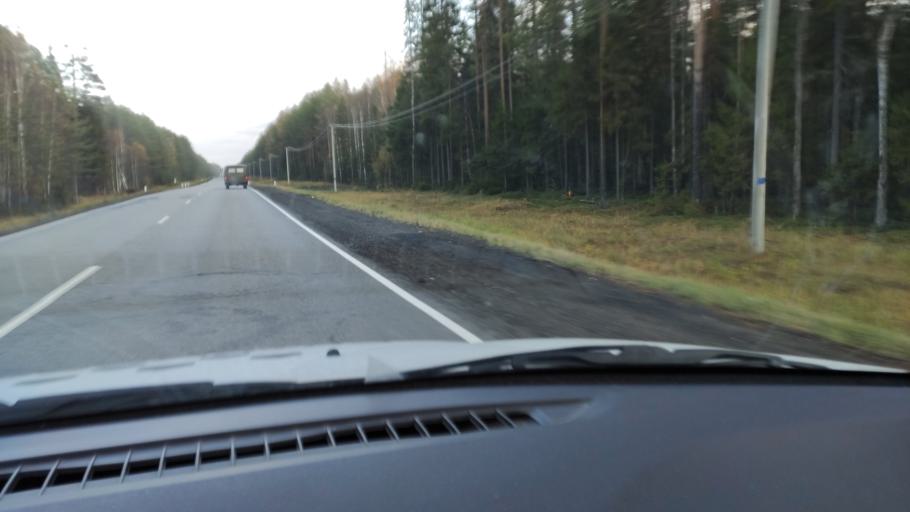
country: RU
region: Kirov
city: Belaya Kholunitsa
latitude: 58.9085
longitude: 50.9917
